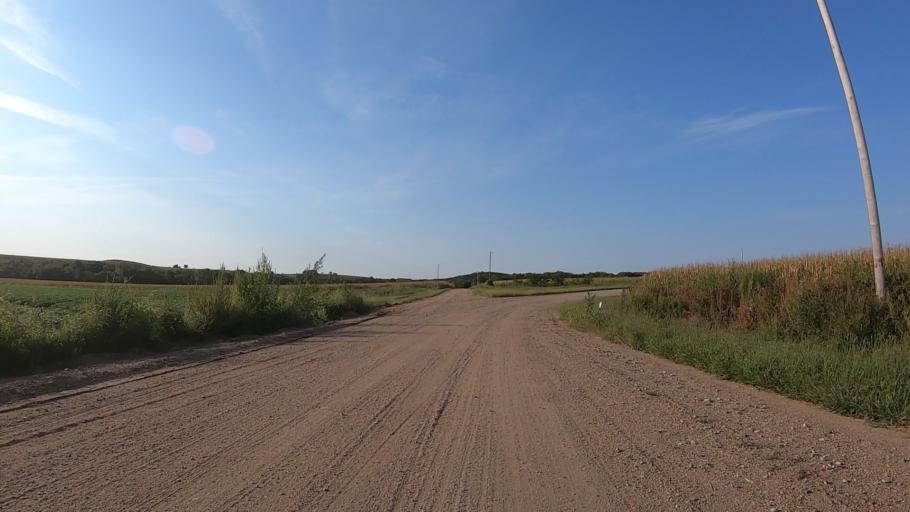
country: US
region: Kansas
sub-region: Marshall County
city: Blue Rapids
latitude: 39.6688
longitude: -96.8066
